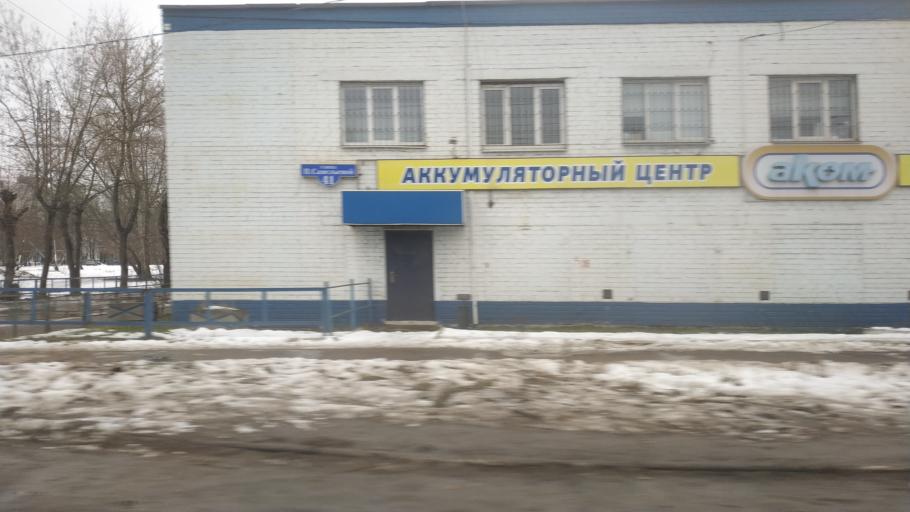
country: RU
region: Tverskaya
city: Tver
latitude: 56.8886
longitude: 35.8352
